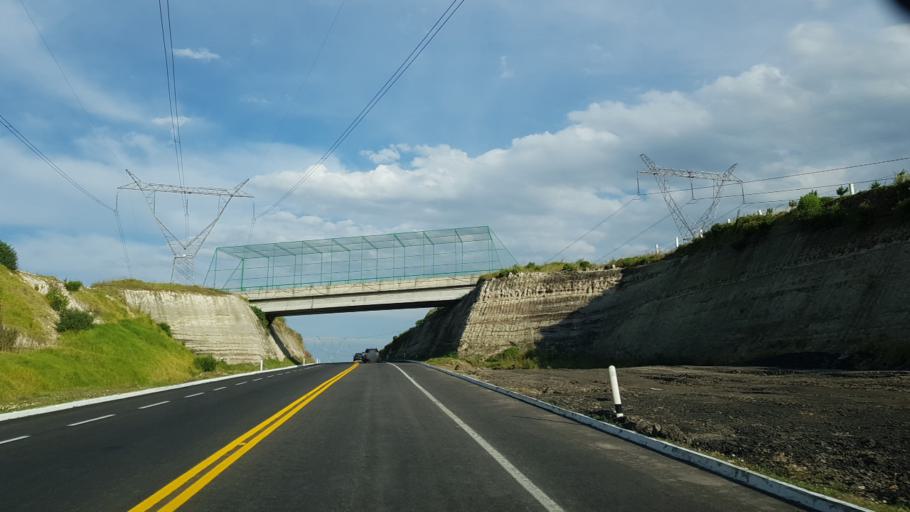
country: MX
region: Mexico
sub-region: Almoloya de Juarez
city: San Pedro de la Hortaliza (Ejido Almoloyan)
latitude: 19.3781
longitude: -99.8501
